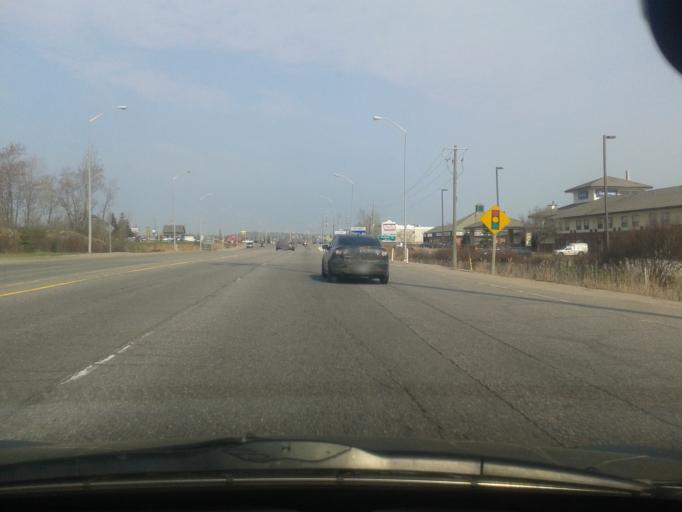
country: CA
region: Ontario
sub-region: Nipissing District
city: North Bay
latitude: 46.3073
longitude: -79.4344
